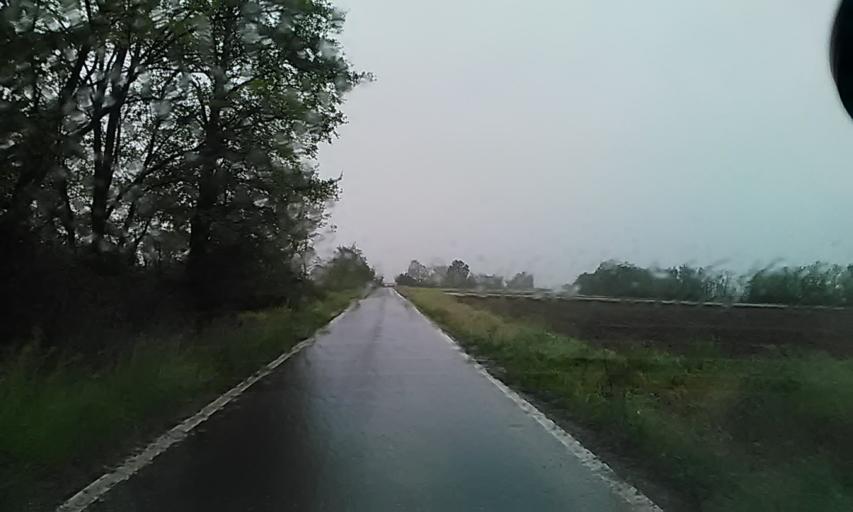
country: IT
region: Piedmont
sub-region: Provincia di Vercelli
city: San Giacomo Vercellese
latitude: 45.4915
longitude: 8.3366
